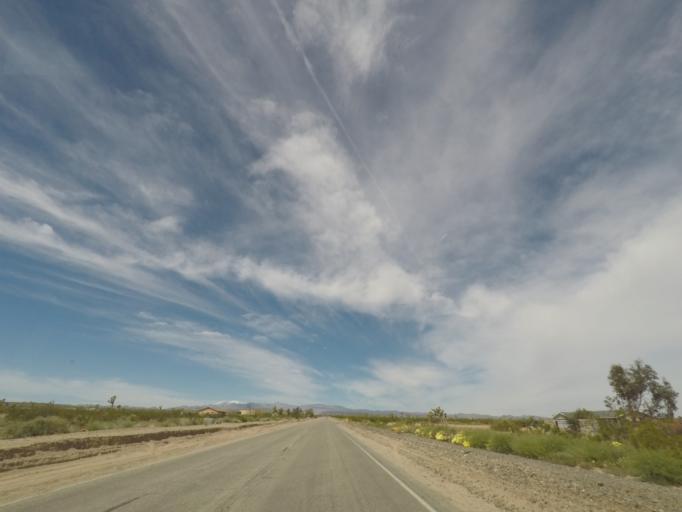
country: US
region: California
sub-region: San Bernardino County
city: Joshua Tree
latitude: 34.1929
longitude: -116.3362
